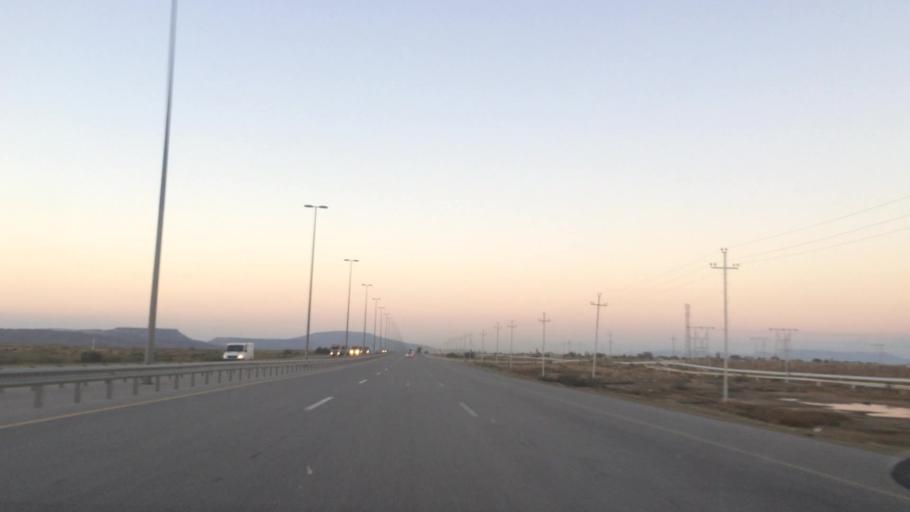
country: AZ
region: Baki
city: Qobustan
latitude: 40.0036
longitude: 49.4291
